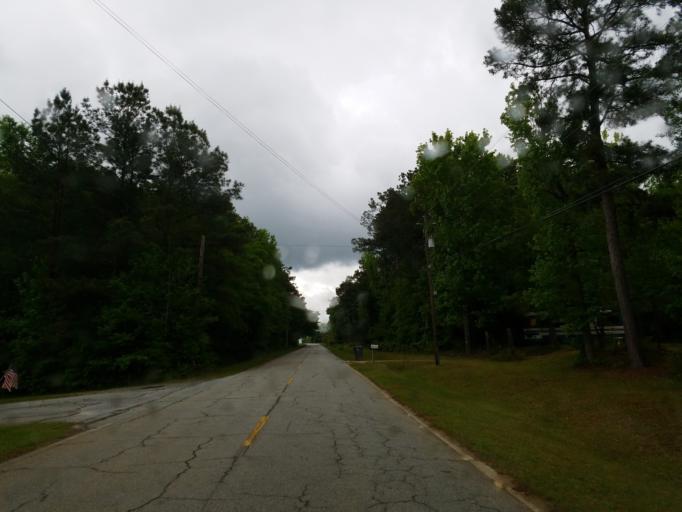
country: US
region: Georgia
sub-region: Lamar County
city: Barnesville
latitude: 33.0949
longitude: -84.1817
